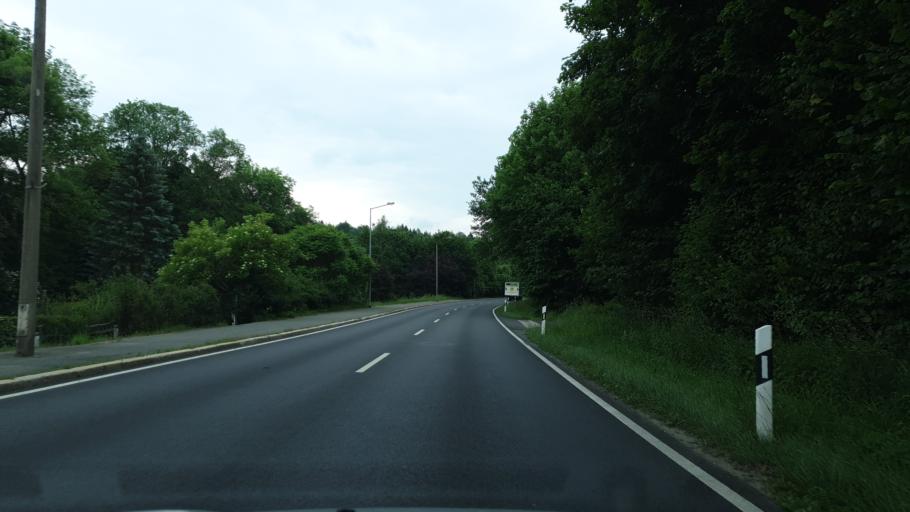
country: DE
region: Saxony
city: Auerbach
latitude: 50.5223
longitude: 12.4004
